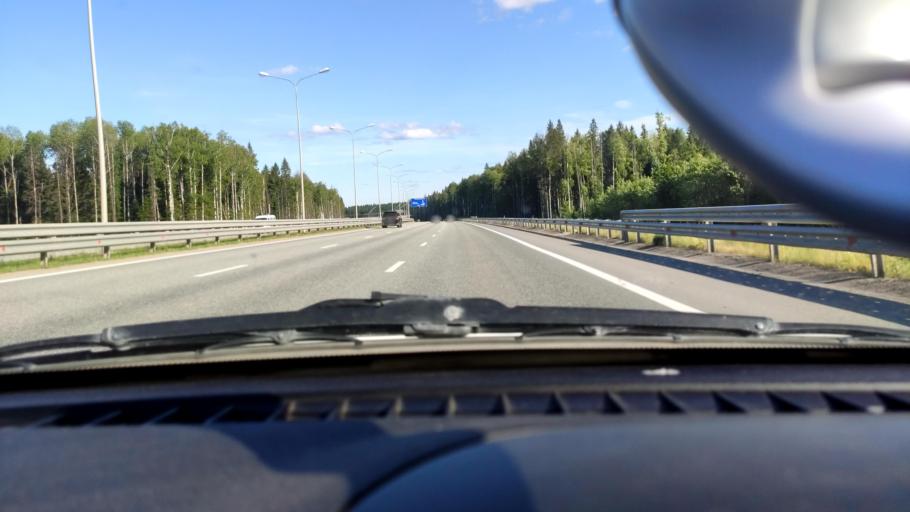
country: RU
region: Perm
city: Bershet'
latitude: 57.7053
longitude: 56.3699
